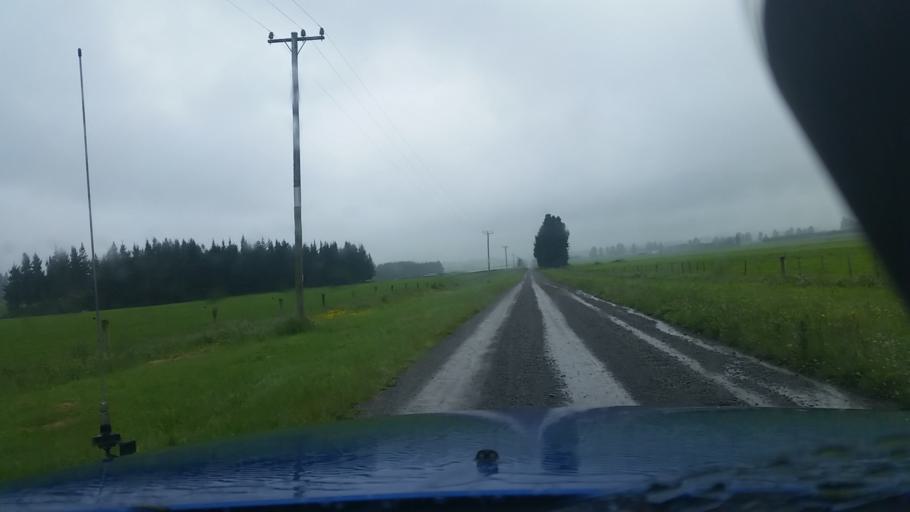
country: NZ
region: Canterbury
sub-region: Ashburton District
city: Methven
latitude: -43.5653
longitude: 171.5410
